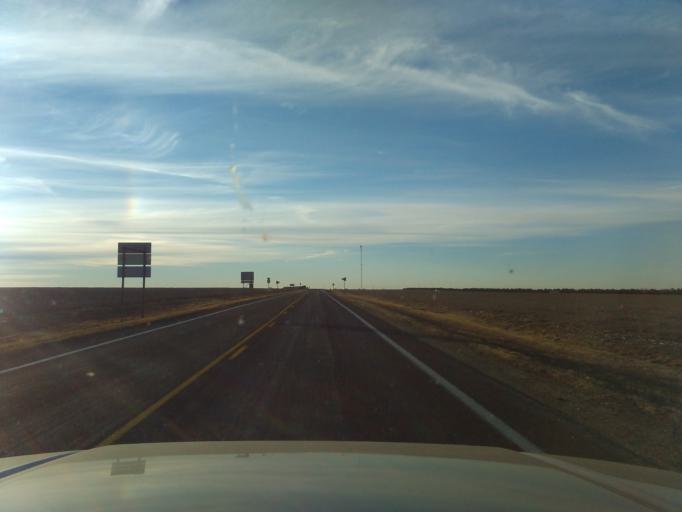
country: US
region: Kansas
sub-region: Logan County
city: Oakley
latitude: 39.1192
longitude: -100.8705
